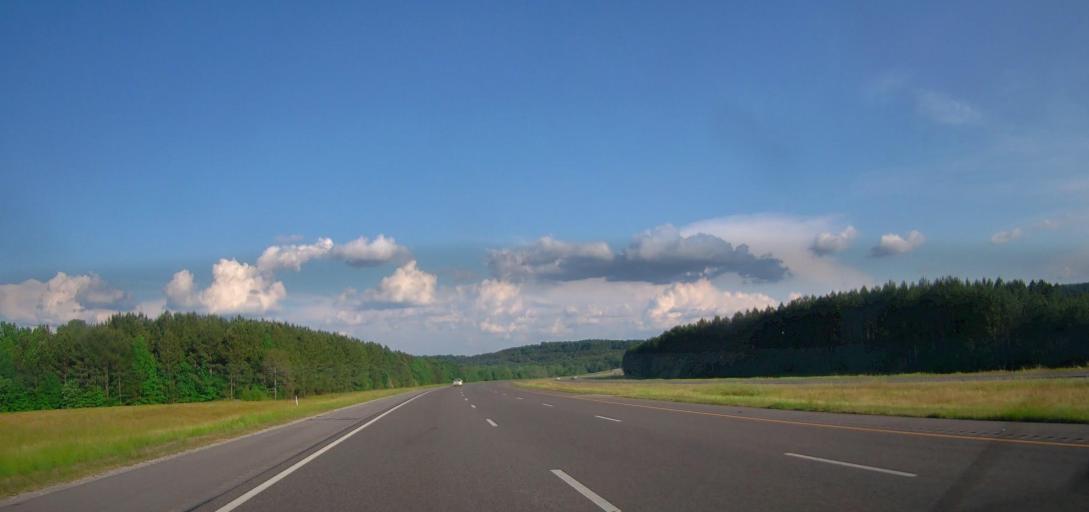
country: US
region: Alabama
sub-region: Walker County
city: Cordova
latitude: 33.7851
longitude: -87.2135
